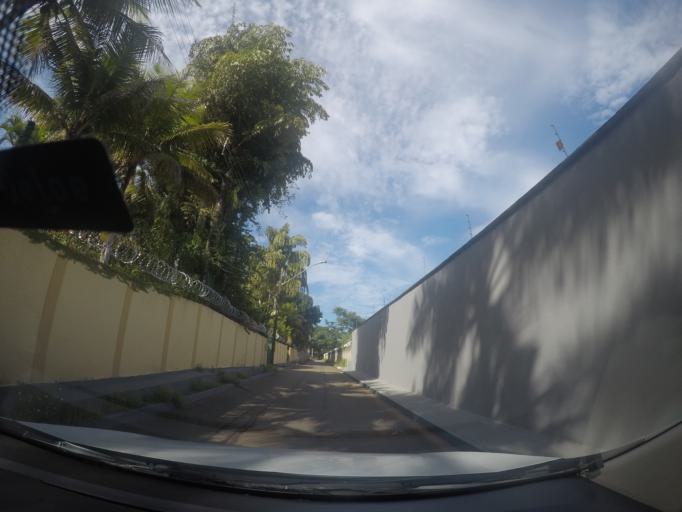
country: BR
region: Goias
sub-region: Goiania
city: Goiania
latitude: -16.6655
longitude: -49.2032
